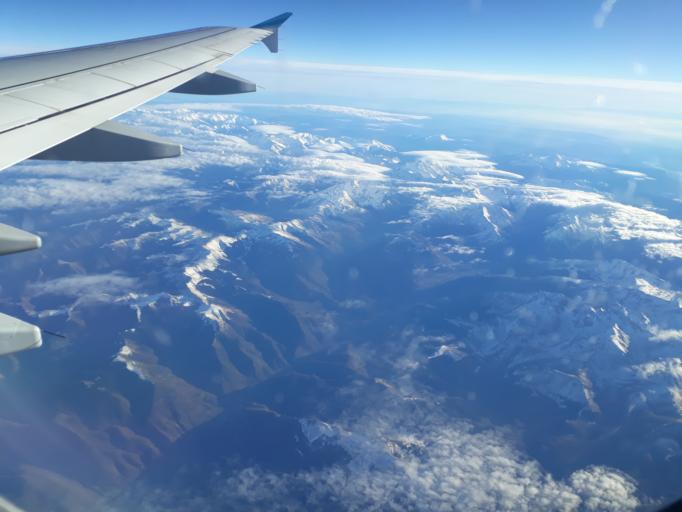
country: FR
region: Midi-Pyrenees
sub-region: Departement des Hautes-Pyrenees
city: Capvern
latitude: 43.0737
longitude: 0.2690
